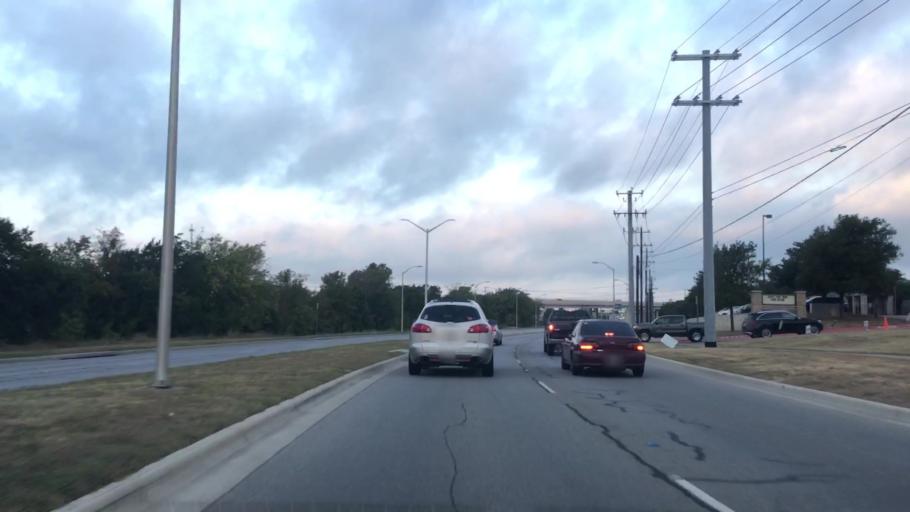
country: US
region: Texas
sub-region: Williamson County
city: Cedar Park
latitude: 30.5029
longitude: -97.8043
